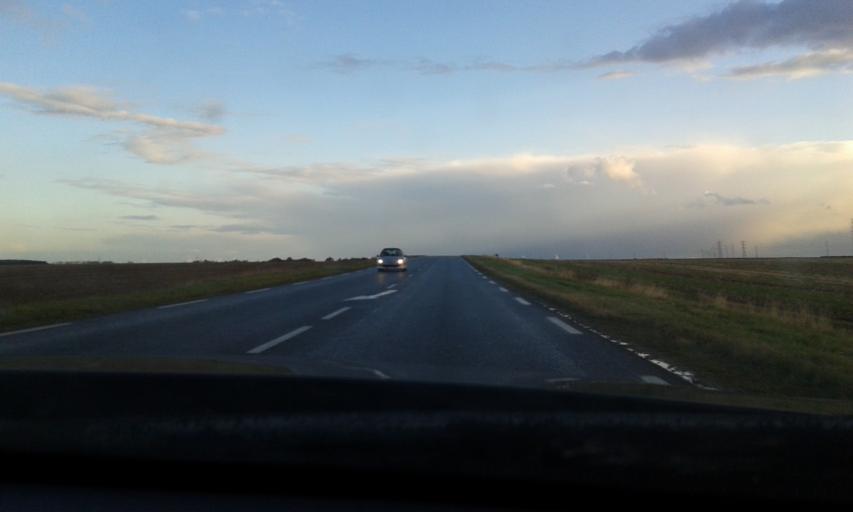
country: FR
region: Centre
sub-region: Departement d'Eure-et-Loir
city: Janville
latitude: 48.2208
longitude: 1.8044
